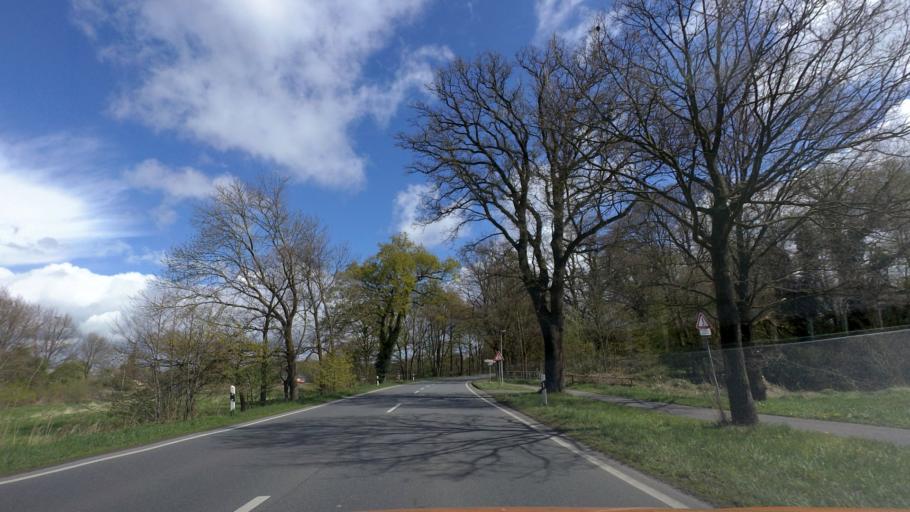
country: DE
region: Lower Saxony
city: Ottersberg
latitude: 53.1054
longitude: 9.1359
